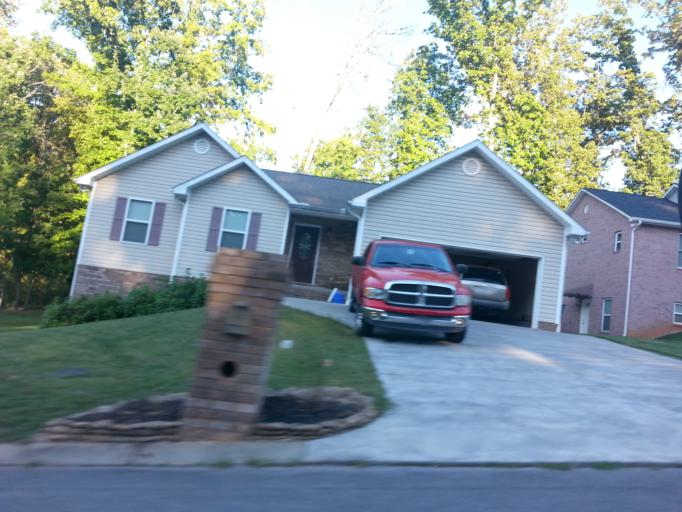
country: US
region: Tennessee
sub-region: Blount County
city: Eagleton Village
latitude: 35.7853
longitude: -83.9312
